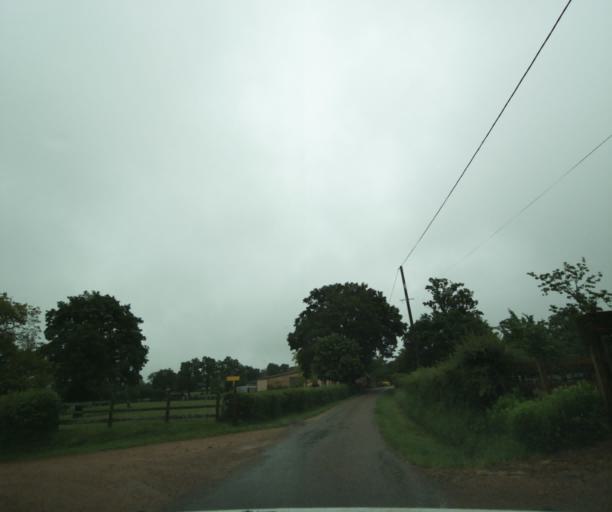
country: FR
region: Bourgogne
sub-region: Departement de Saone-et-Loire
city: Charolles
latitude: 46.4300
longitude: 4.3595
